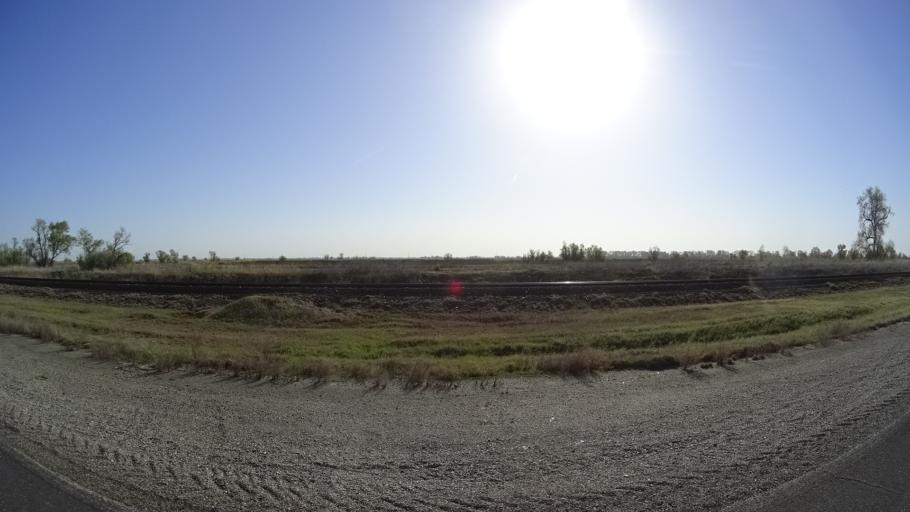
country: US
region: California
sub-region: Glenn County
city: Willows
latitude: 39.4022
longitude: -122.1925
